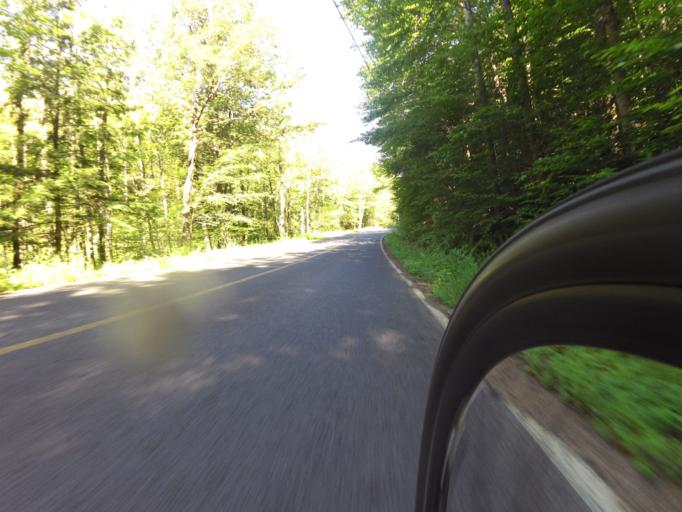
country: CA
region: Quebec
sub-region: Laurentides
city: Brownsburg-Chatham
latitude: 45.8870
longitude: -74.5853
